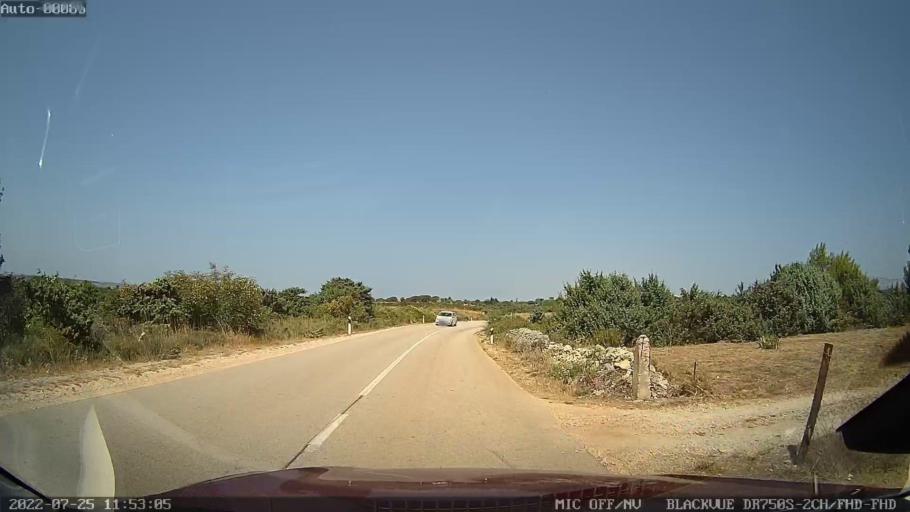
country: HR
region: Zadarska
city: Vrsi
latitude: 44.2529
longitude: 15.2368
